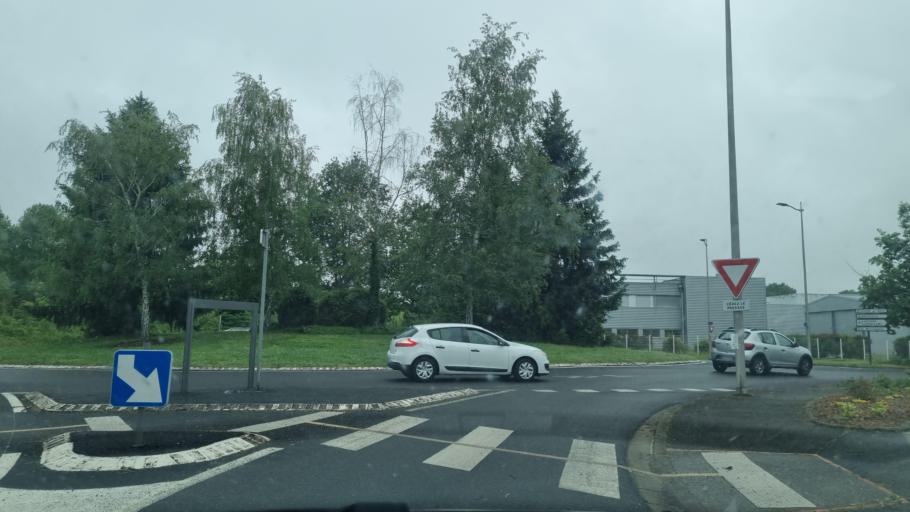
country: FR
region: Aquitaine
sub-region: Departement des Pyrenees-Atlantiques
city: Idron
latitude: 43.3204
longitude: -0.3272
